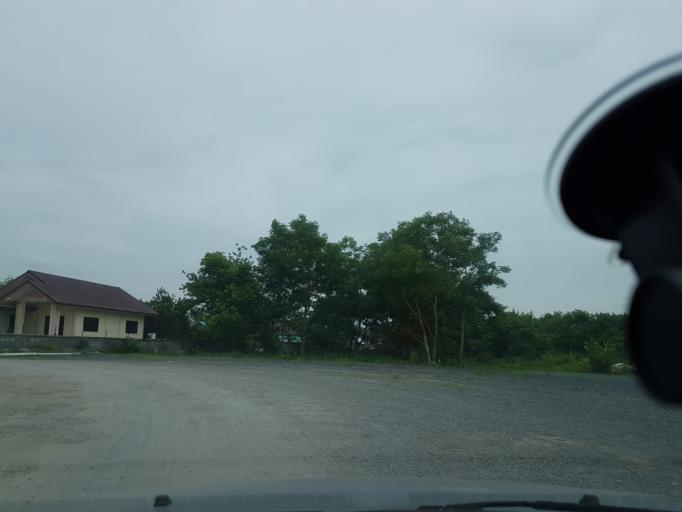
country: TH
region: Lop Buri
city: Lop Buri
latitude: 14.7718
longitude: 100.6902
